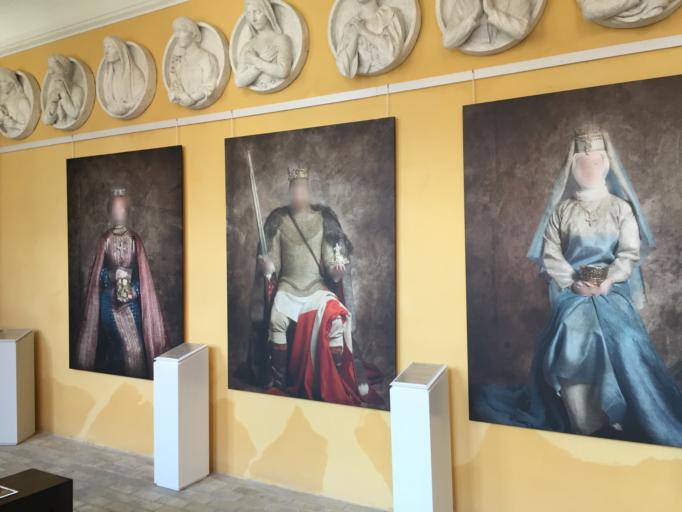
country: DK
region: South Denmark
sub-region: Nyborg Kommune
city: Nyborg
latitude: 55.3113
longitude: 10.7884
